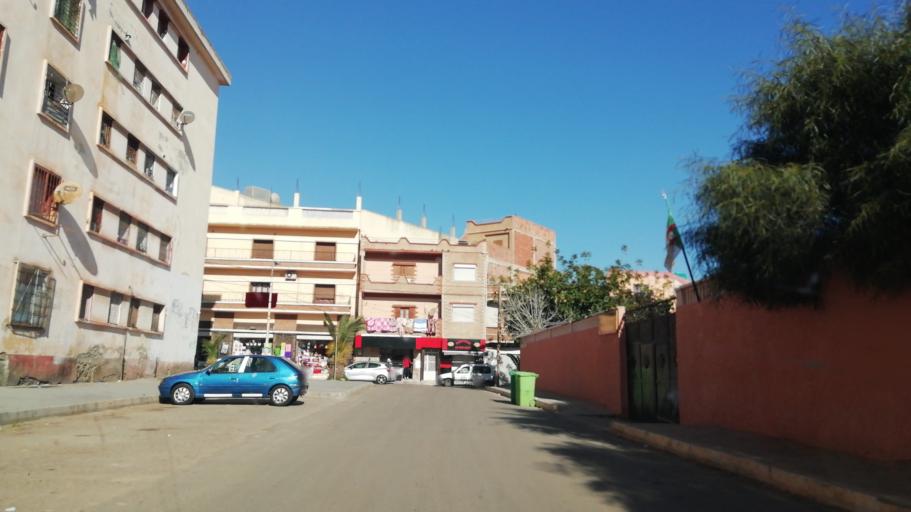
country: DZ
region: Oran
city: Oran
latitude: 35.6736
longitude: -0.6494
